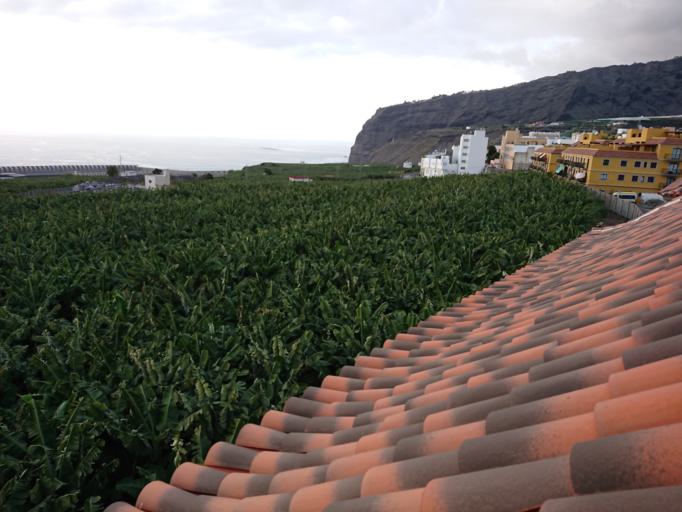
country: ES
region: Canary Islands
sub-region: Provincia de Santa Cruz de Tenerife
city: Tazacorte
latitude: 28.6385
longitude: -17.9330
